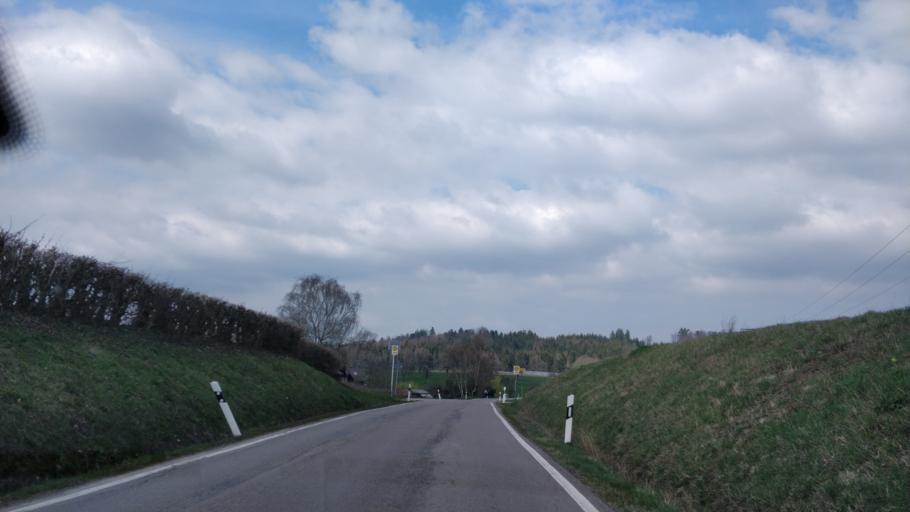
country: DE
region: Baden-Wuerttemberg
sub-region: Regierungsbezirk Stuttgart
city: Murrhardt
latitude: 49.0051
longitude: 9.5635
